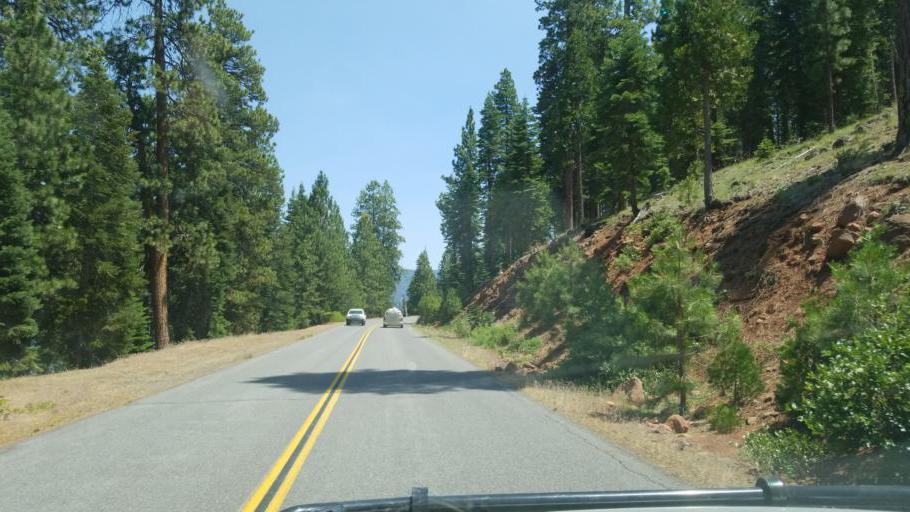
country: US
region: California
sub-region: Lassen County
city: Susanville
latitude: 40.5605
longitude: -120.8298
